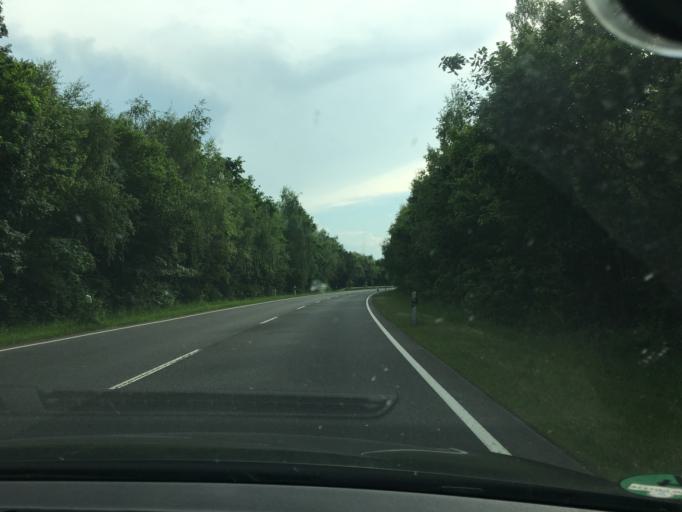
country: DE
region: North Rhine-Westphalia
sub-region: Regierungsbezirk Koln
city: Nideggen
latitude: 50.7046
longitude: 6.5406
